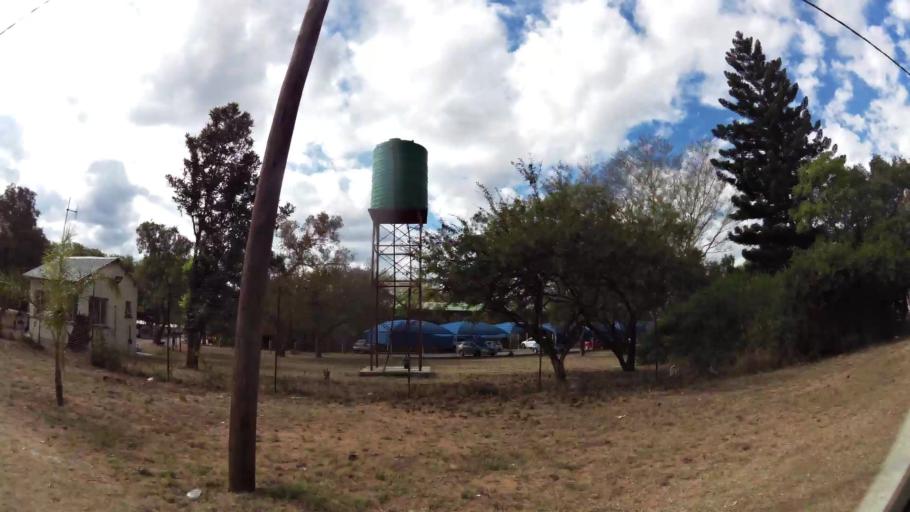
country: ZA
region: Limpopo
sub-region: Waterberg District Municipality
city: Modimolle
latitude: -24.7059
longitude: 28.4009
